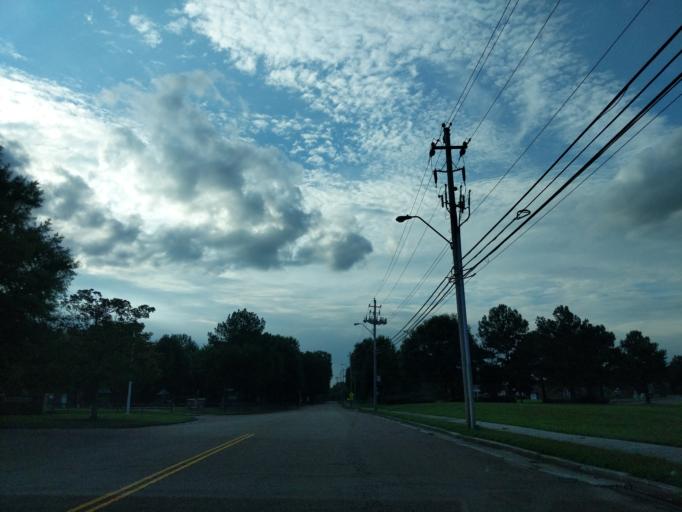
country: US
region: Tennessee
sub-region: Shelby County
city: Germantown
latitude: 35.0644
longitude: -89.7671
